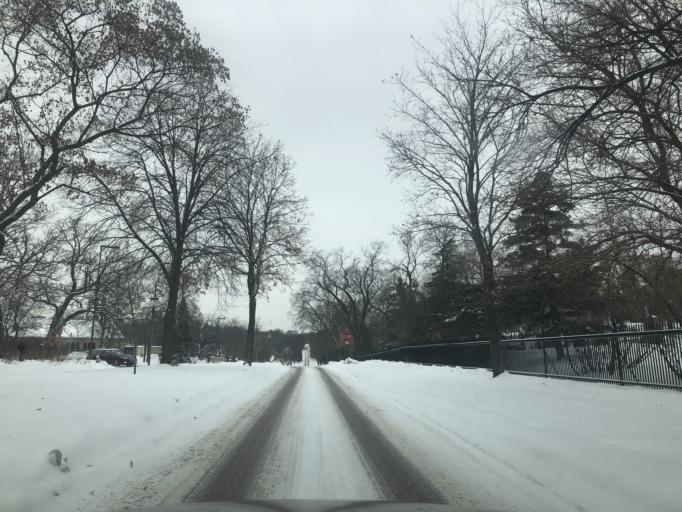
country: US
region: Minnesota
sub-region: Hennepin County
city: Richfield
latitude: 44.9347
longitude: -93.2935
